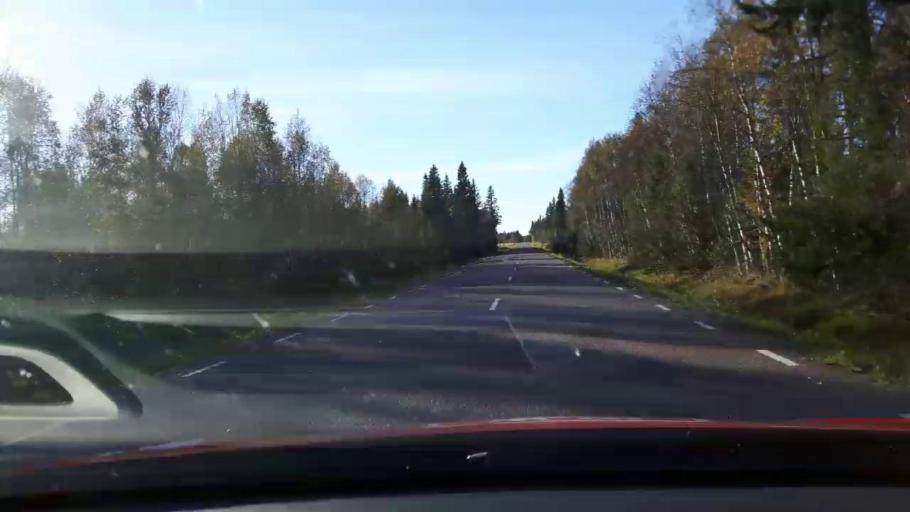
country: SE
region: Jaemtland
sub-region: Stroemsunds Kommun
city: Stroemsund
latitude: 63.8619
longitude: 15.1692
